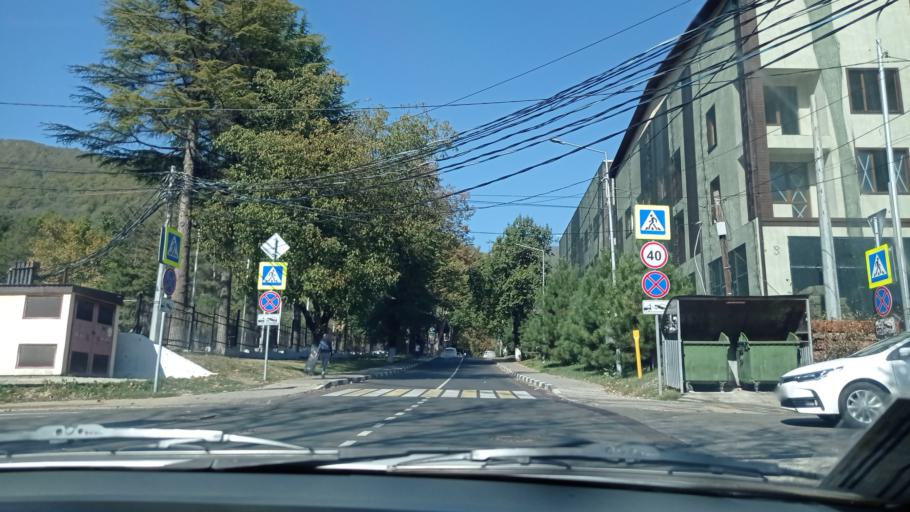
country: RU
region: Krasnodarskiy
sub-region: Sochi City
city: Krasnaya Polyana
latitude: 43.6770
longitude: 40.2040
